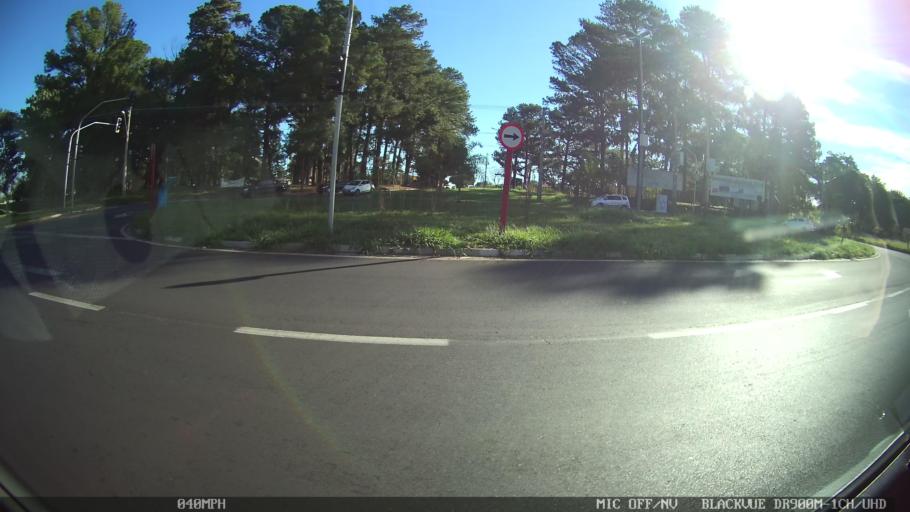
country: BR
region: Sao Paulo
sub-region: Araraquara
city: Araraquara
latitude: -21.7528
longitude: -48.1821
